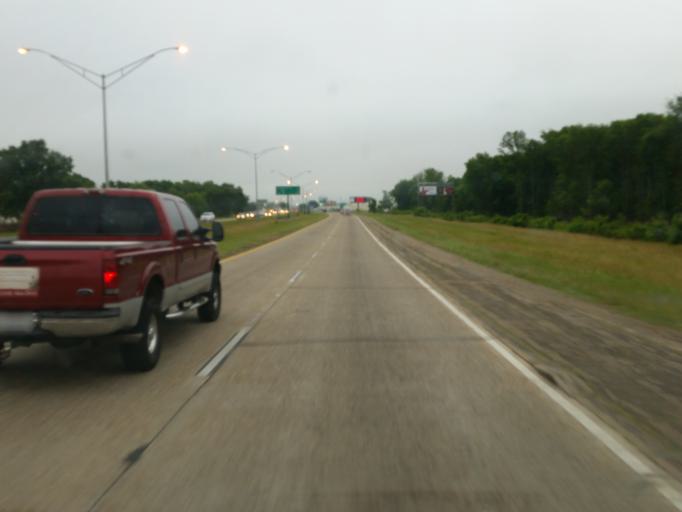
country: US
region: Louisiana
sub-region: Bossier Parish
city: Bossier City
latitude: 32.5261
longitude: -93.6883
